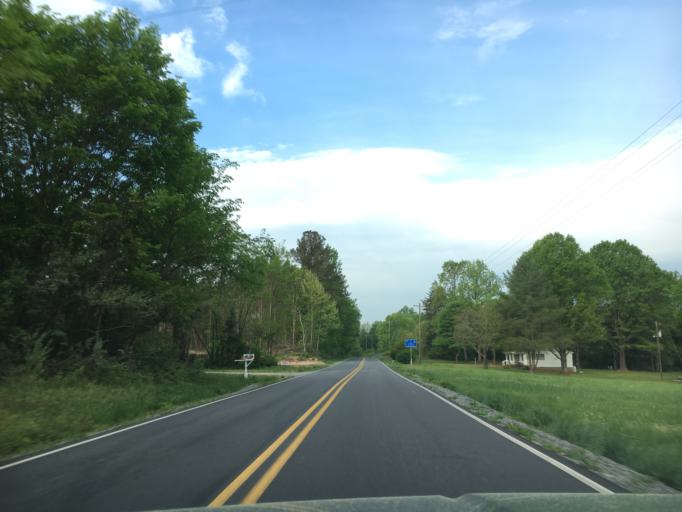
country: US
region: Virginia
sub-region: Halifax County
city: Halifax
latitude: 36.8921
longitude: -78.8333
